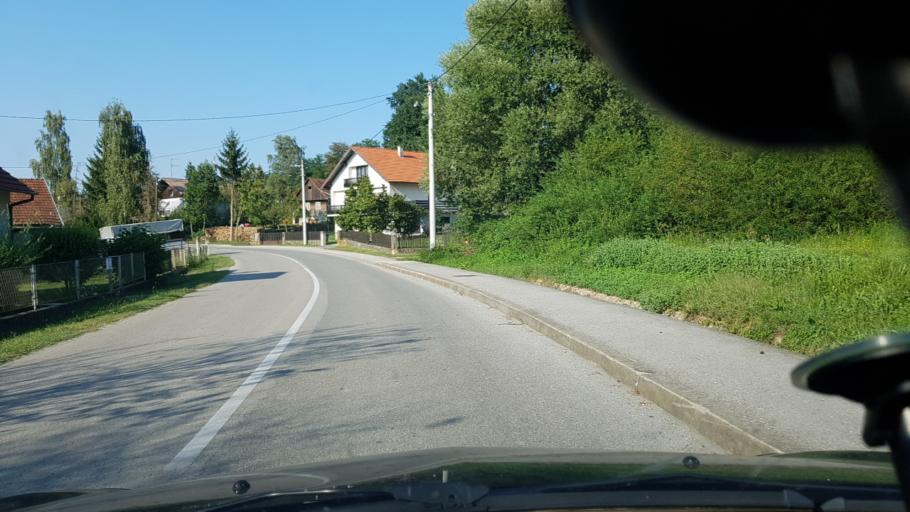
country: HR
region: Zagrebacka
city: Pojatno
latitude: 45.9491
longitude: 15.7325
